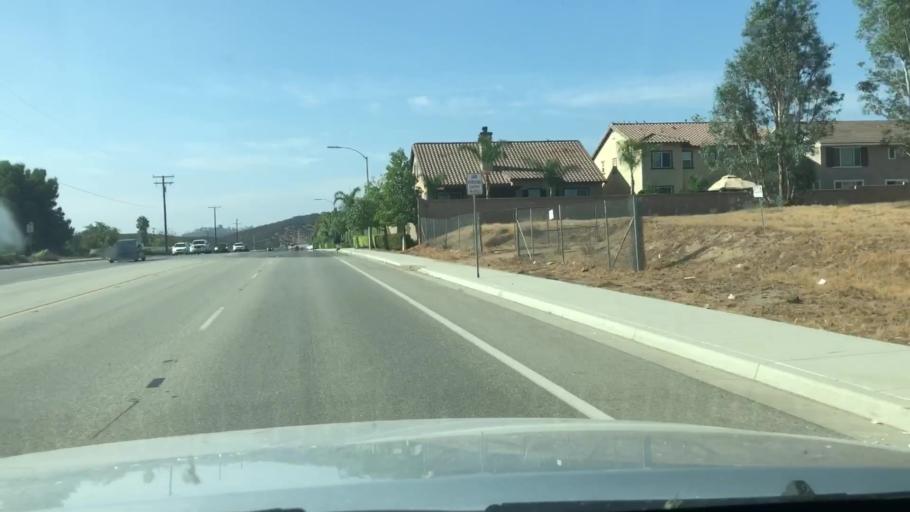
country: US
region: California
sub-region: Riverside County
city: Murrieta Hot Springs
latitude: 33.6025
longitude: -117.1630
